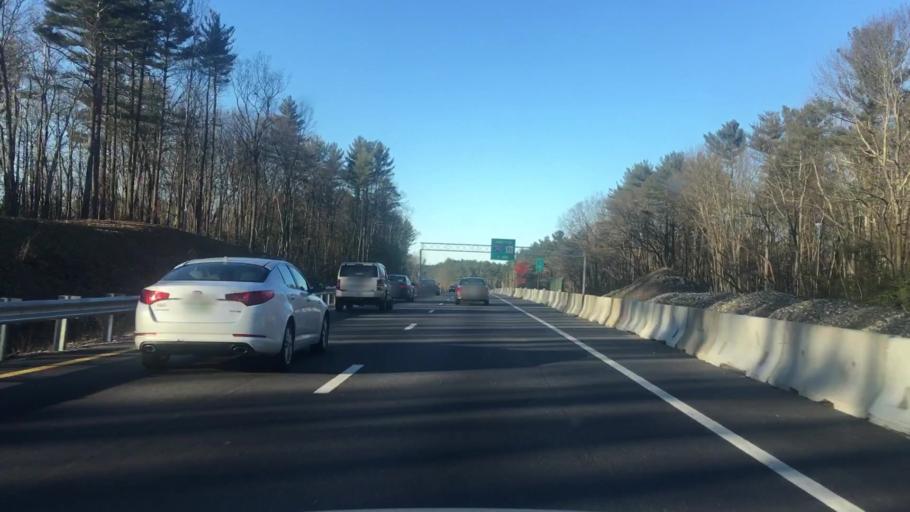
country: US
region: New Hampshire
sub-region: Rockingham County
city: Londonderry
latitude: 42.9310
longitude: -71.3802
